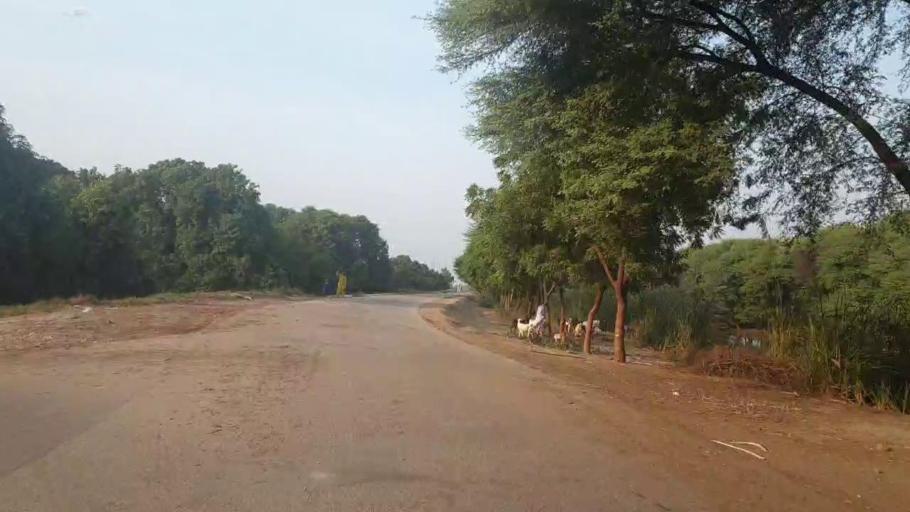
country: PK
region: Sindh
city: Tando Jam
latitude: 25.4486
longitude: 68.5849
